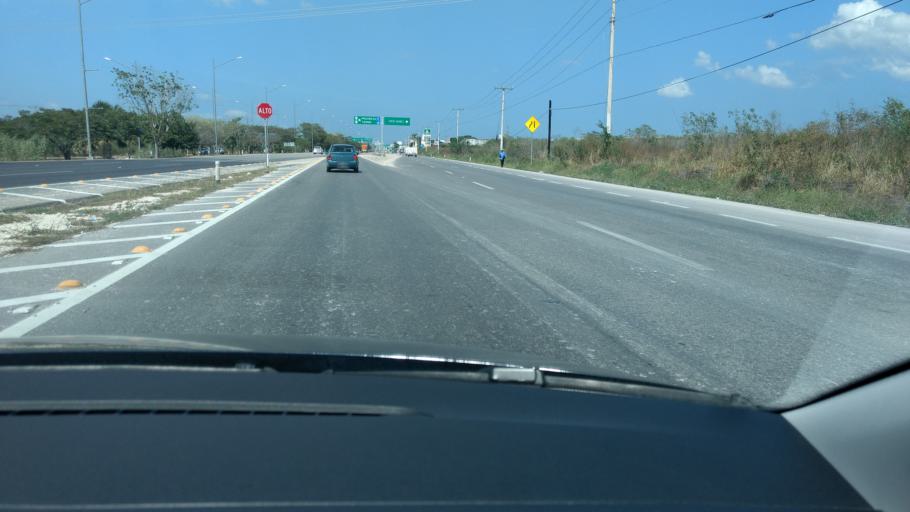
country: MX
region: Yucatan
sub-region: Kanasin
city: Kanasin
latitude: 20.9859
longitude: -89.5630
